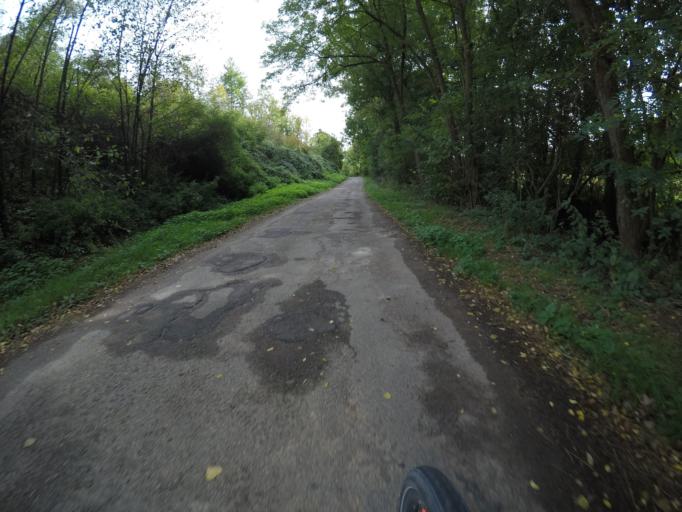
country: DE
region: Baden-Wuerttemberg
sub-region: Karlsruhe Region
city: Oberderdingen
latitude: 49.0973
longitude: 8.7525
